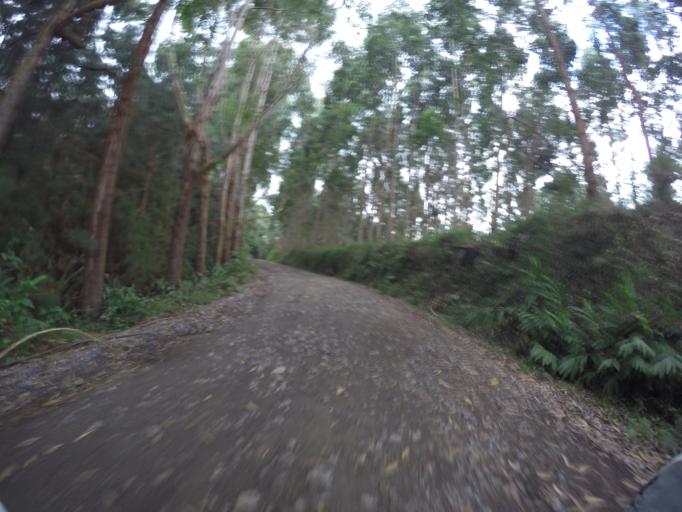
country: CO
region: Quindio
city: Filandia
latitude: 4.7172
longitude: -75.6282
